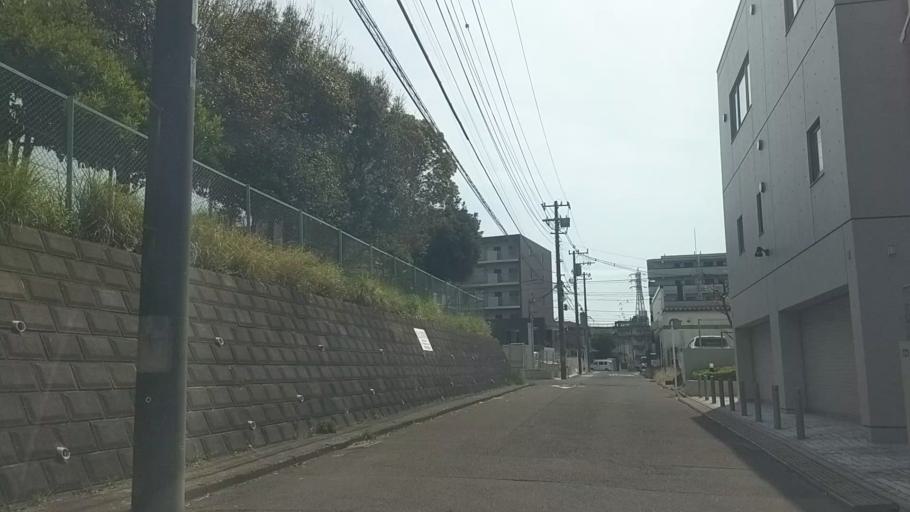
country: JP
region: Kanagawa
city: Kamakura
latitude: 35.3712
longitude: 139.5786
